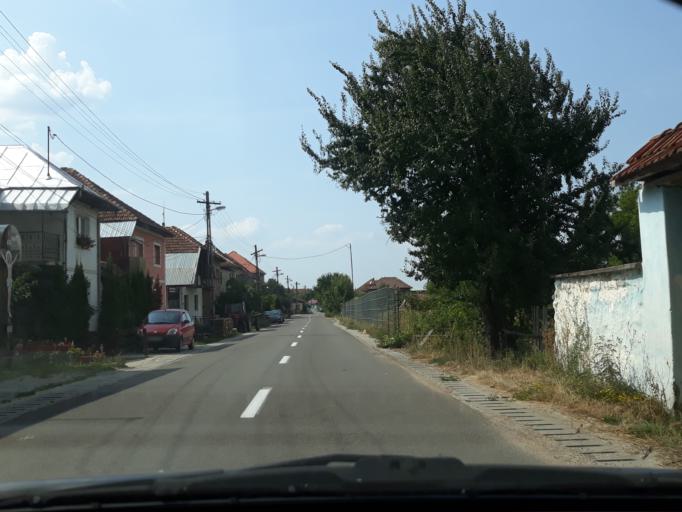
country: RO
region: Bihor
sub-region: Comuna Pietroasa
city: Pietroasa
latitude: 46.5902
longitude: 22.5611
